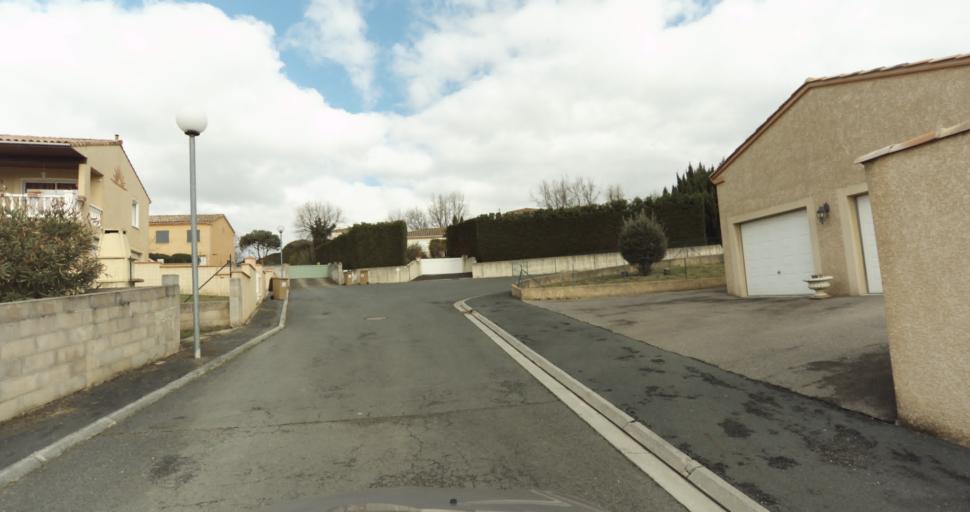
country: FR
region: Midi-Pyrenees
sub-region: Departement du Tarn
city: Frejairolles
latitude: 43.8703
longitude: 2.1956
